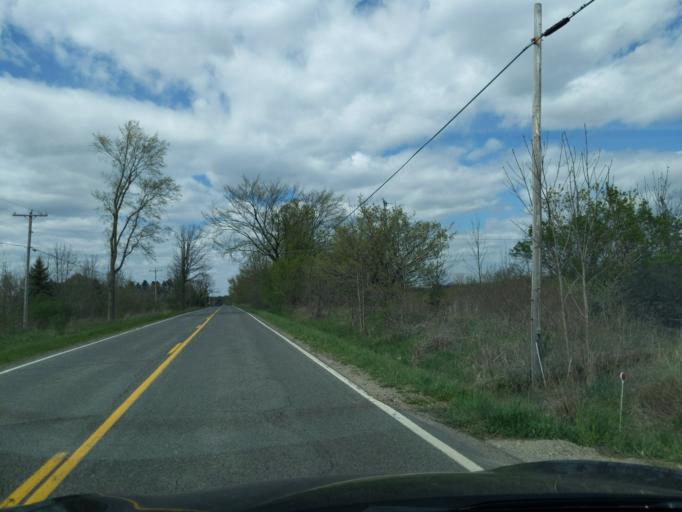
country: US
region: Michigan
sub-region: Ingham County
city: Mason
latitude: 42.6198
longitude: -84.4574
